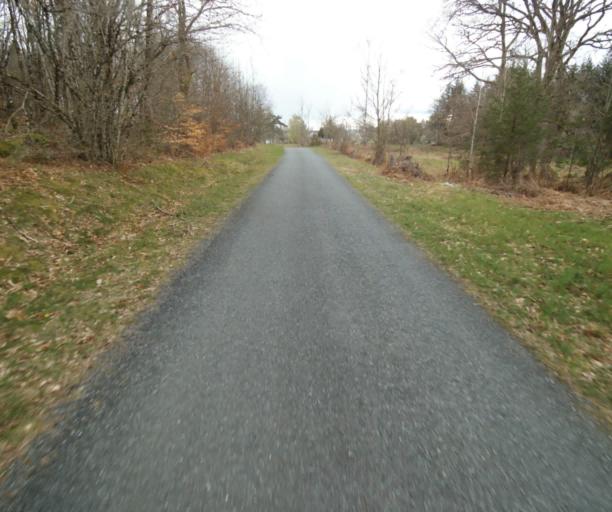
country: FR
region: Limousin
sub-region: Departement de la Correze
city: Correze
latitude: 45.2933
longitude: 1.9242
